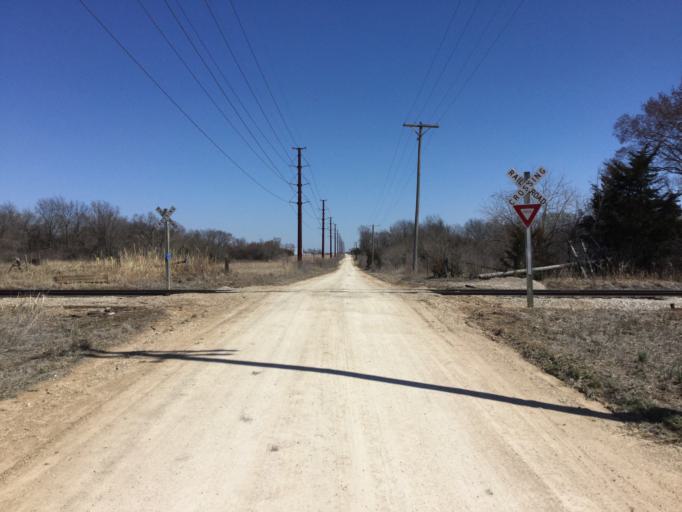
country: US
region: Kansas
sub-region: Allen County
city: Humboldt
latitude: 37.7765
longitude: -95.4297
